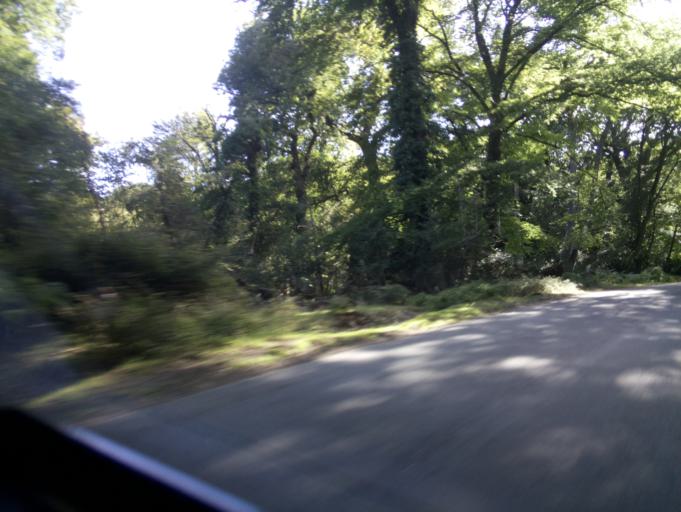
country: GB
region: England
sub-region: Hampshire
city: Cadnam
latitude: 50.9363
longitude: -1.6343
